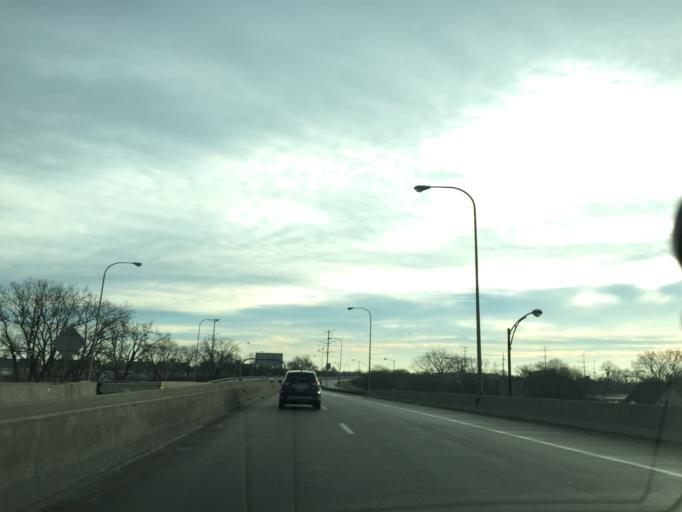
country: US
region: Illinois
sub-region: Cook County
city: Chicago
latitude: 41.7749
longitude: -87.6258
